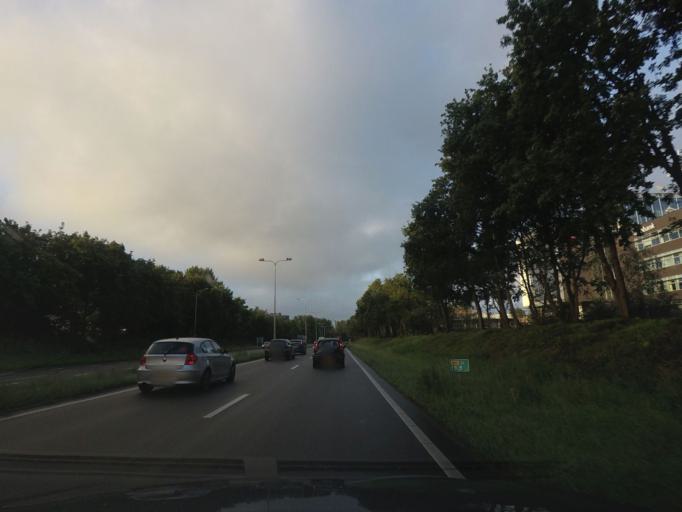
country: NL
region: North Holland
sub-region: Gemeente Alkmaar
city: Alkmaar
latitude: 52.6397
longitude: 4.7250
